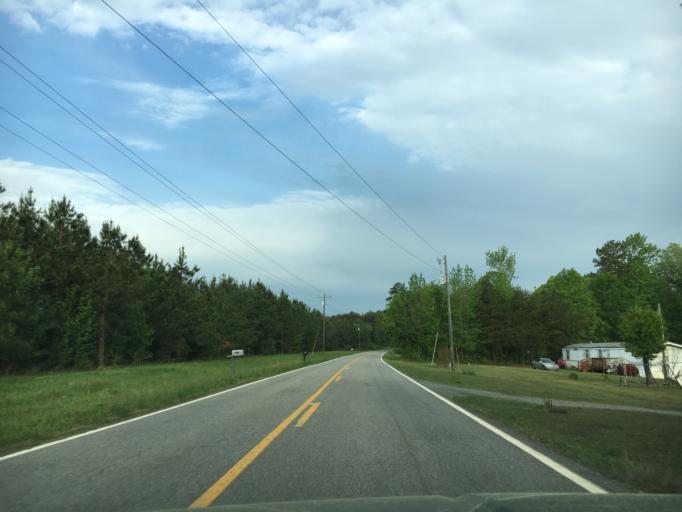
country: US
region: Virginia
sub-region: Halifax County
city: Halifax
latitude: 36.8909
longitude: -78.8081
